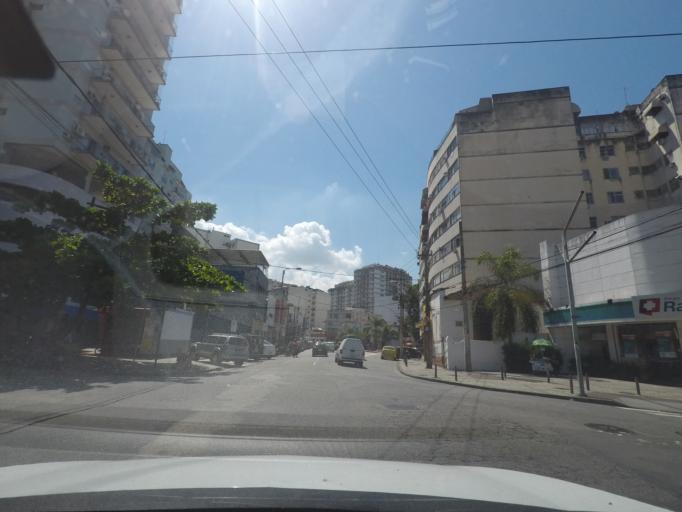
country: BR
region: Rio de Janeiro
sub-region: Rio De Janeiro
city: Rio de Janeiro
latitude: -22.9239
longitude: -43.2558
